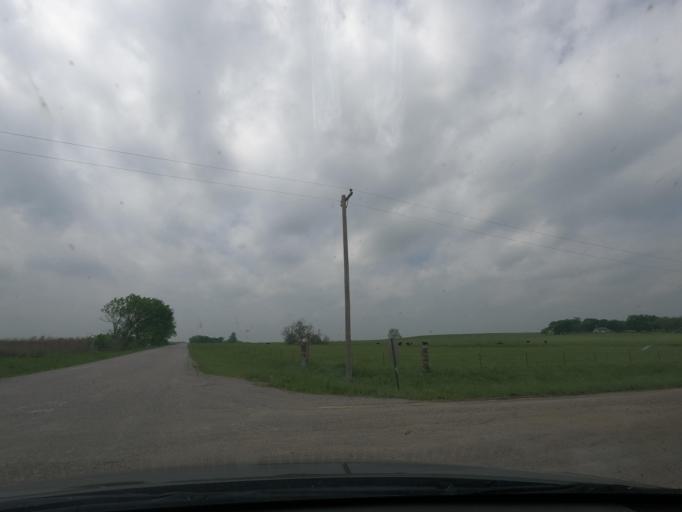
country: US
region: Kansas
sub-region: Cherokee County
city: Columbus
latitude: 37.2817
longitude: -94.9589
